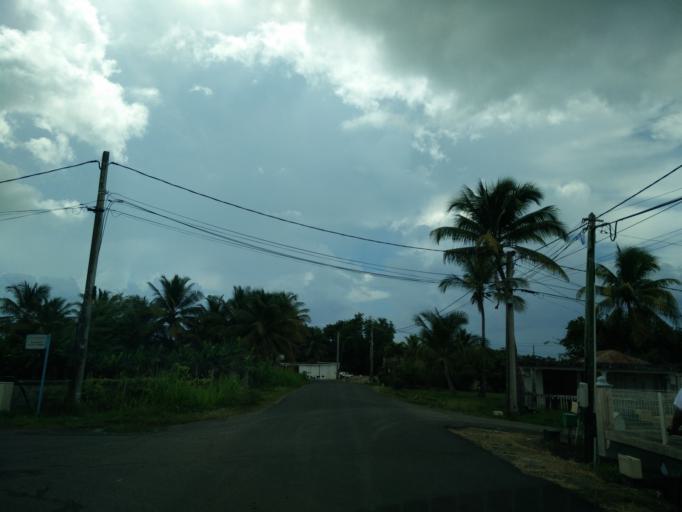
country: GP
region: Guadeloupe
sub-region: Guadeloupe
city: Le Moule
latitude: 16.2762
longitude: -61.3426
